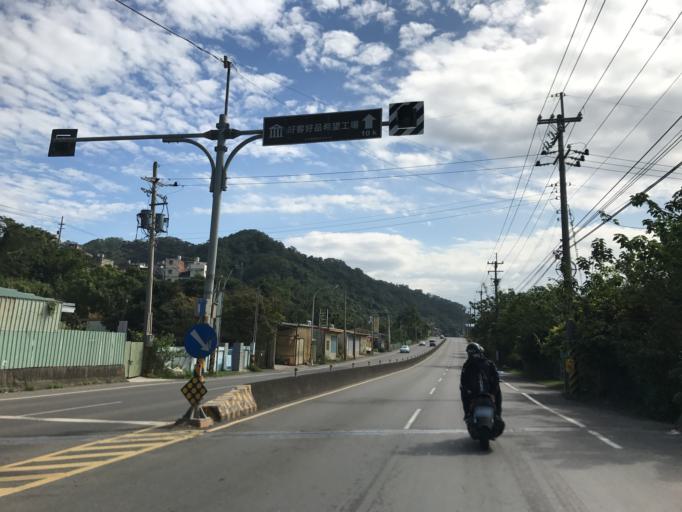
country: TW
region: Taiwan
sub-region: Hsinchu
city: Zhubei
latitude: 24.7455
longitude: 121.1023
